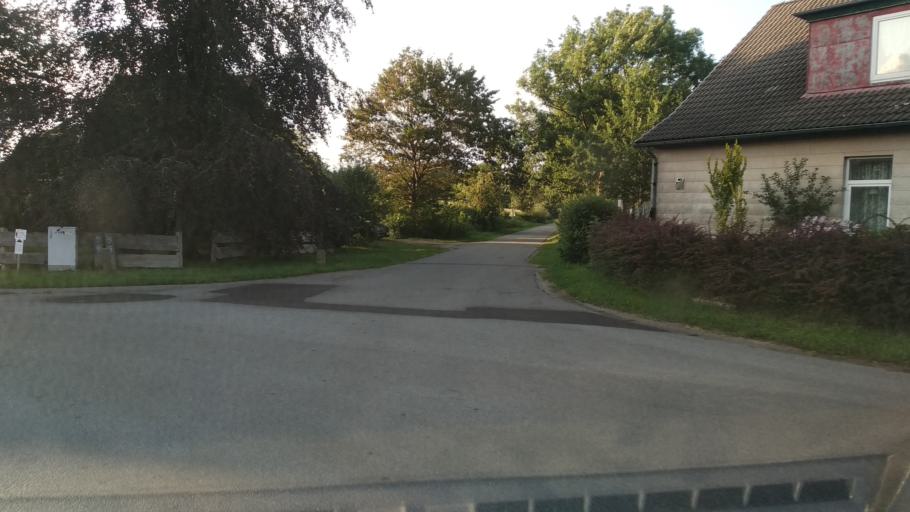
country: DE
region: Schleswig-Holstein
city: Klein Bennebek
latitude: 54.4197
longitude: 9.4561
